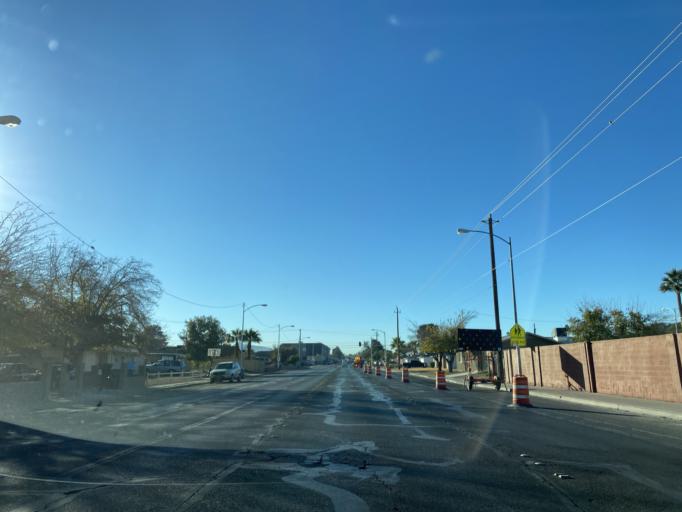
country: US
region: Nevada
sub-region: Clark County
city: Winchester
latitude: 36.1265
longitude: -115.0920
